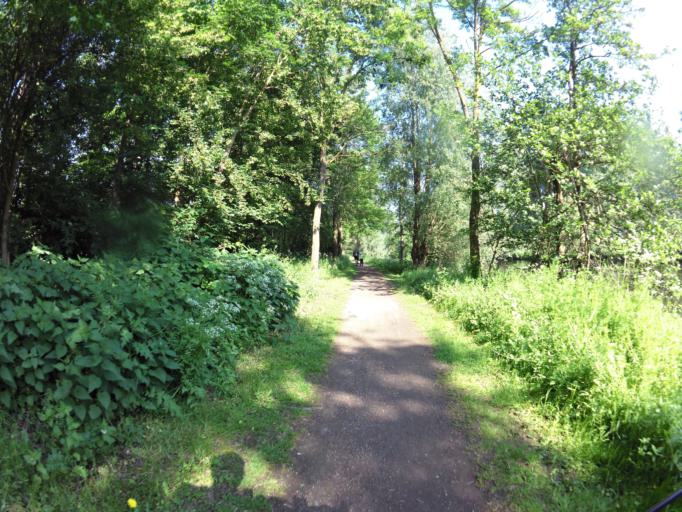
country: DE
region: North Rhine-Westphalia
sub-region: Regierungsbezirk Koln
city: Linnich
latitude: 50.9648
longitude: 6.2828
